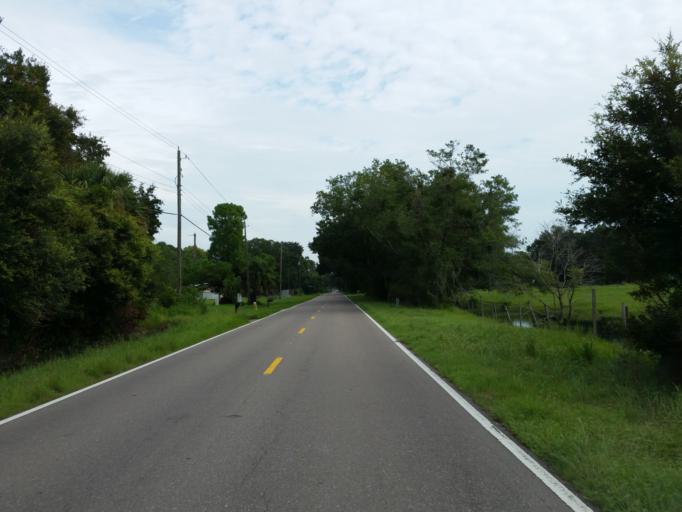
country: US
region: Florida
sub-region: Hillsborough County
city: Dover
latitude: 28.0414
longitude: -82.2366
